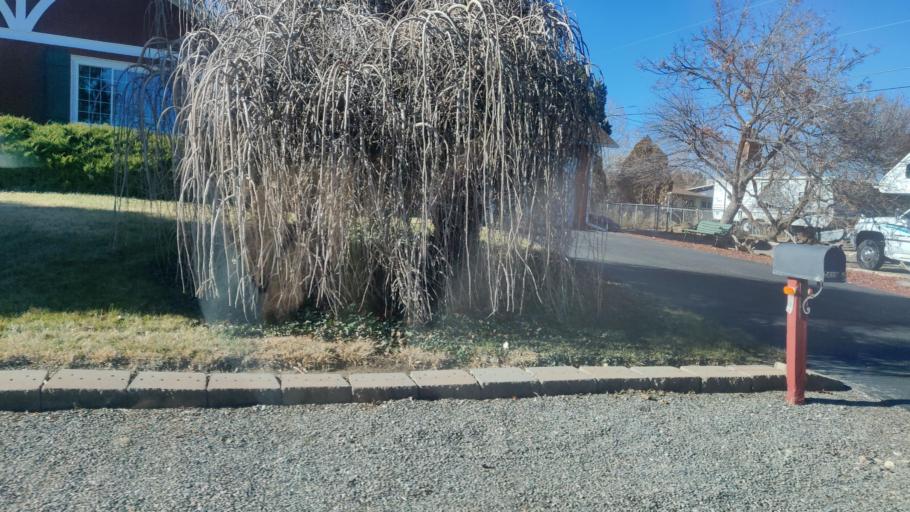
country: US
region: Colorado
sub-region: Mesa County
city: Grand Junction
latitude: 39.0658
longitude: -108.5922
